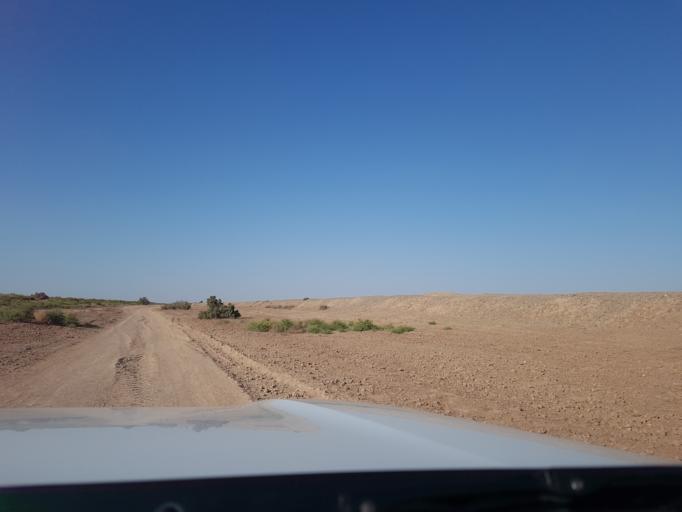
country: IR
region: Razavi Khorasan
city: Sarakhs
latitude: 36.9685
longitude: 61.3834
